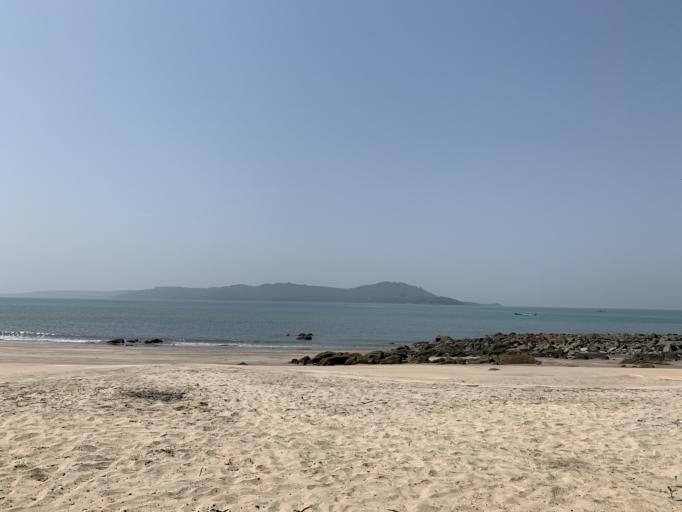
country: GN
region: Conakry
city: Camayenne
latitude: 9.5047
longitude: -13.7673
